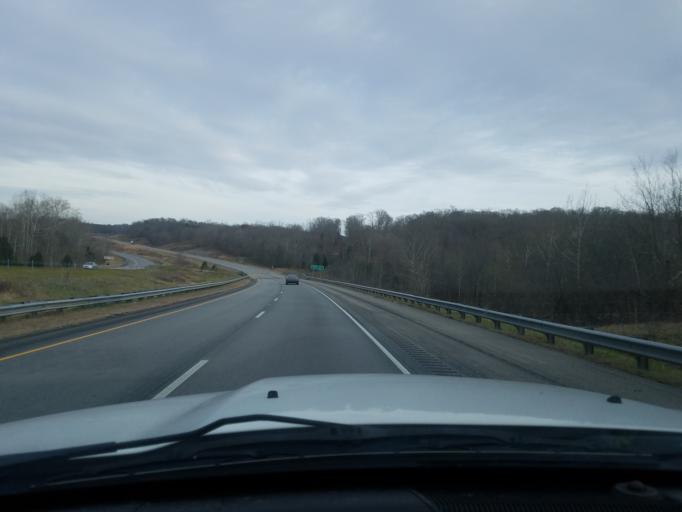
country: US
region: Indiana
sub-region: Crawford County
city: English
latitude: 38.2267
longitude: -86.6392
